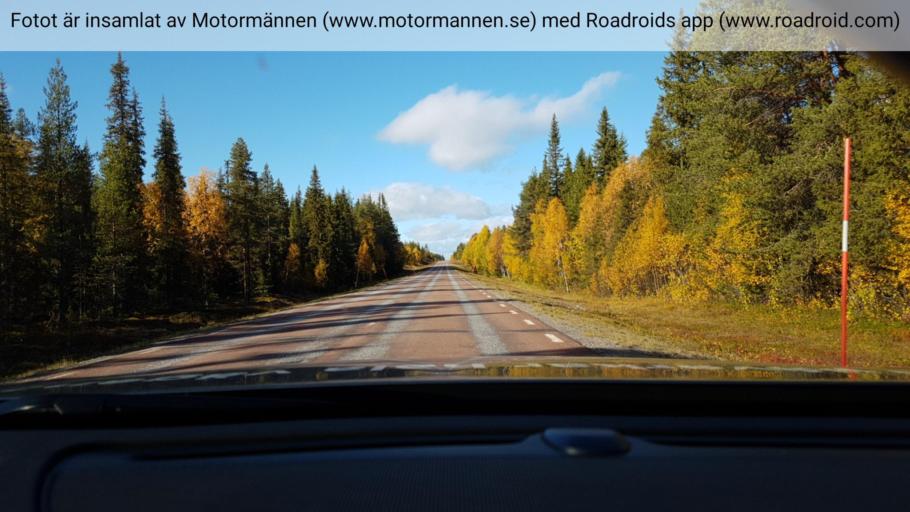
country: SE
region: Norrbotten
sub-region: Arjeplogs Kommun
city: Arjeplog
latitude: 66.0544
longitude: 17.9980
